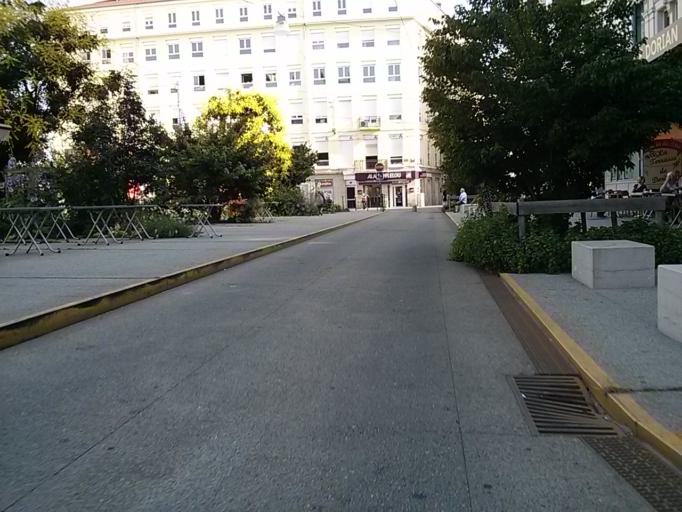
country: FR
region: Rhone-Alpes
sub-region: Departement de la Loire
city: Saint-Etienne
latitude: 45.4380
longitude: 4.3887
